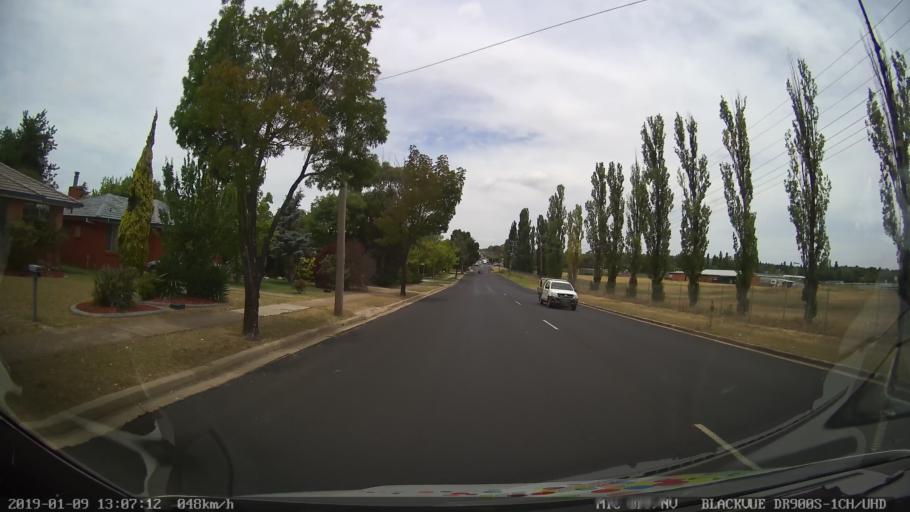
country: AU
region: New South Wales
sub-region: Armidale Dumaresq
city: Armidale
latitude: -30.5180
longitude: 151.6802
